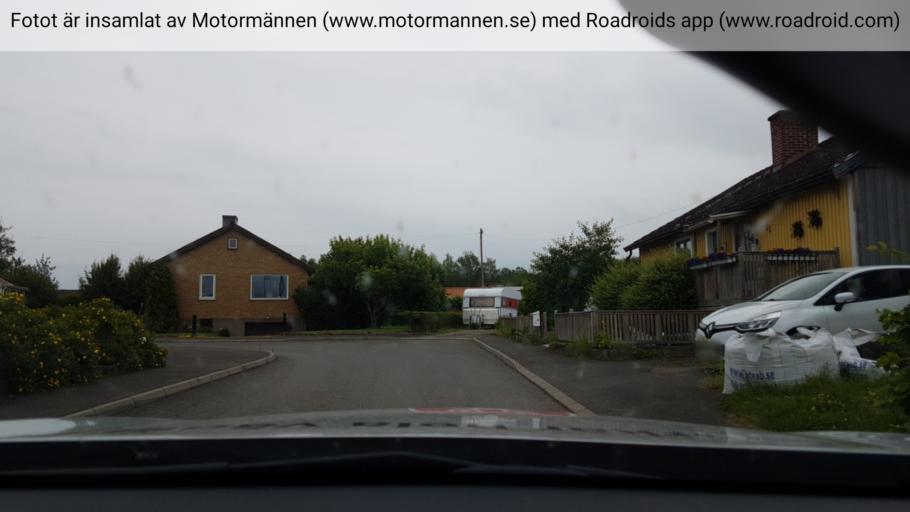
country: SE
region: Vaestra Goetaland
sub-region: Skovde Kommun
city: Skoevde
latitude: 58.3835
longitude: 13.8694
